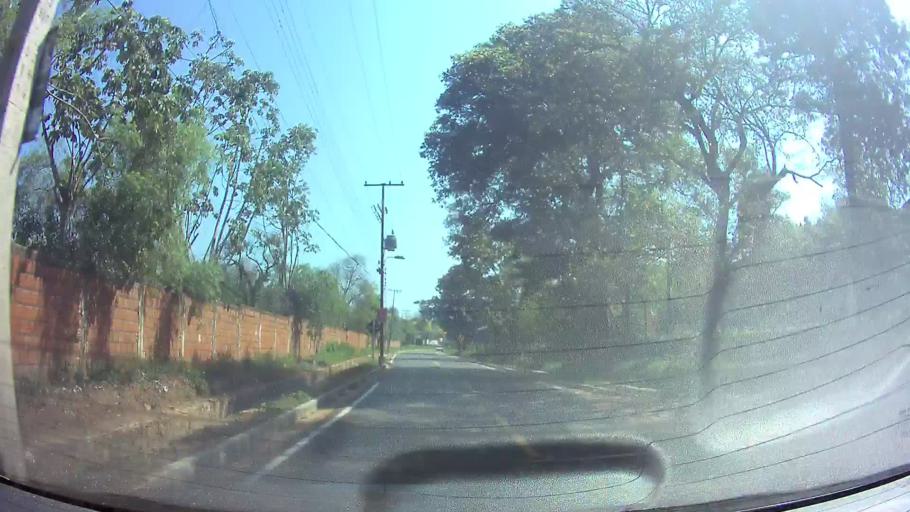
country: PY
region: Central
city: Limpio
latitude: -25.2372
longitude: -57.4992
